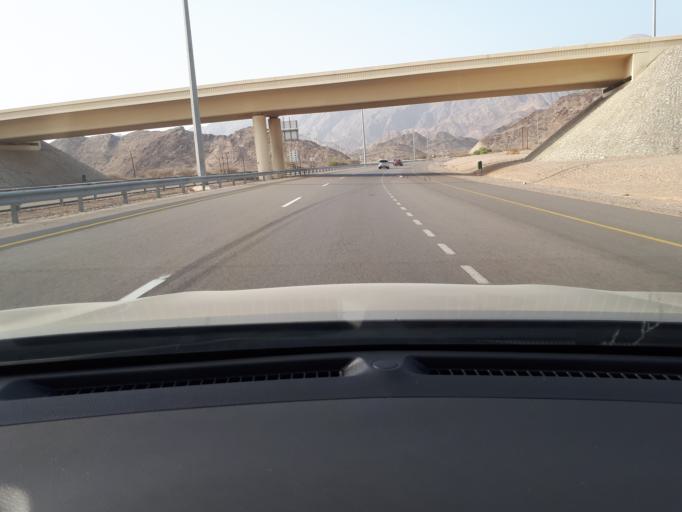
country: OM
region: Muhafazat Masqat
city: Muscat
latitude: 23.3100
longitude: 58.7295
